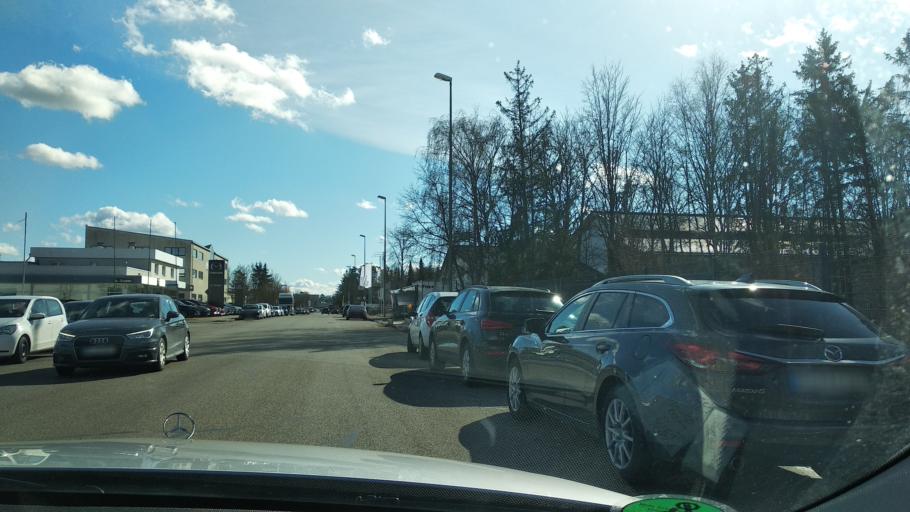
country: DE
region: Bavaria
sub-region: Upper Bavaria
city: Waldkraiburg
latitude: 48.2146
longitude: 12.4110
